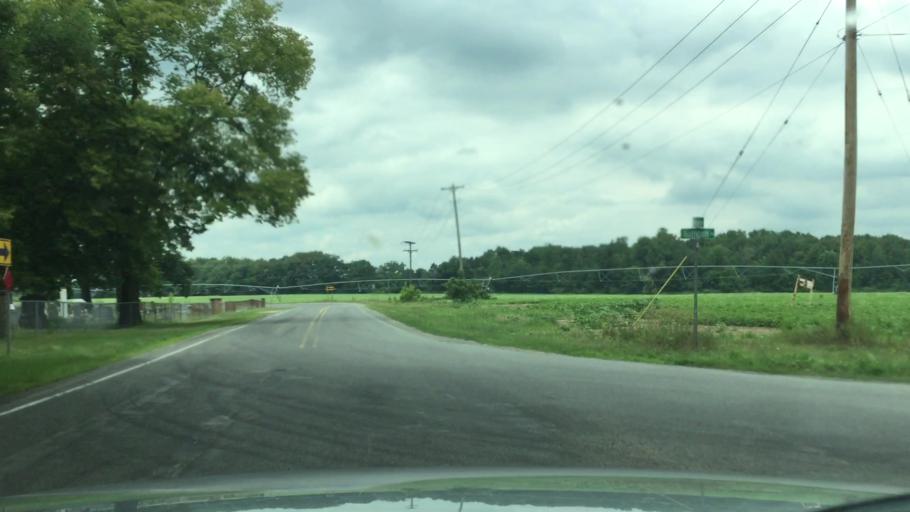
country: US
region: Michigan
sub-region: Saginaw County
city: Burt
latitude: 43.2800
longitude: -83.8872
